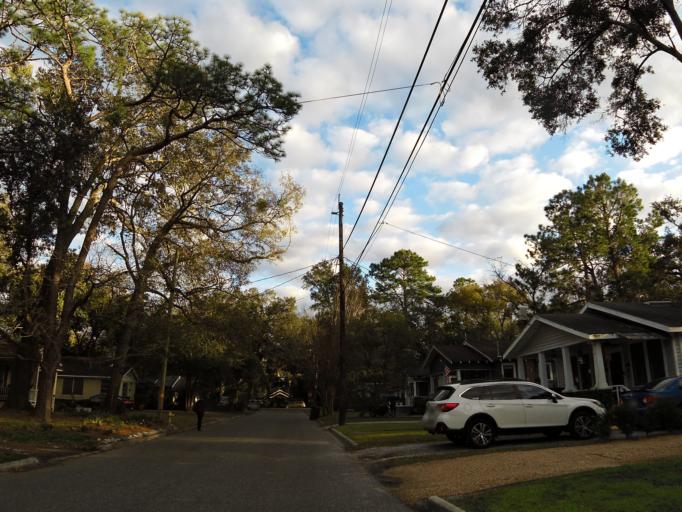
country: US
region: Florida
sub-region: Duval County
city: Jacksonville
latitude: 30.3003
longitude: -81.7123
